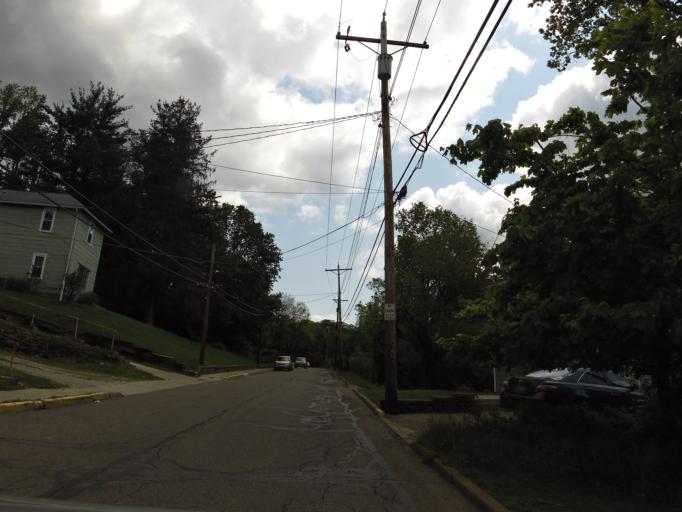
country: US
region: Ohio
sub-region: Athens County
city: Athens
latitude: 39.3327
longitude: -82.1094
